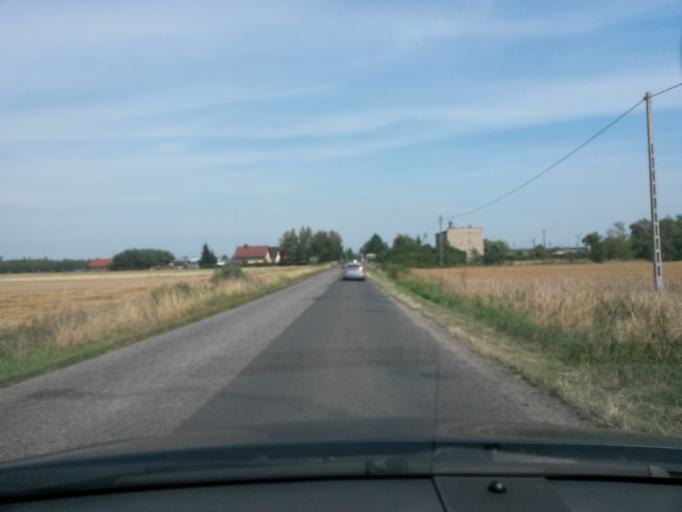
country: PL
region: Lower Silesian Voivodeship
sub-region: Powiat legnicki
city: Prochowice
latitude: 51.2539
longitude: 16.3630
